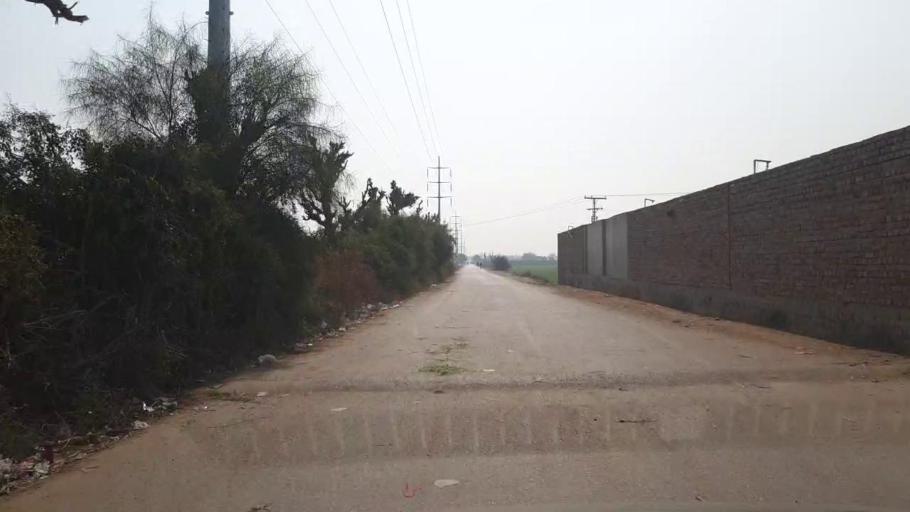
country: PK
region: Sindh
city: Hala
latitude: 25.8327
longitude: 68.4202
